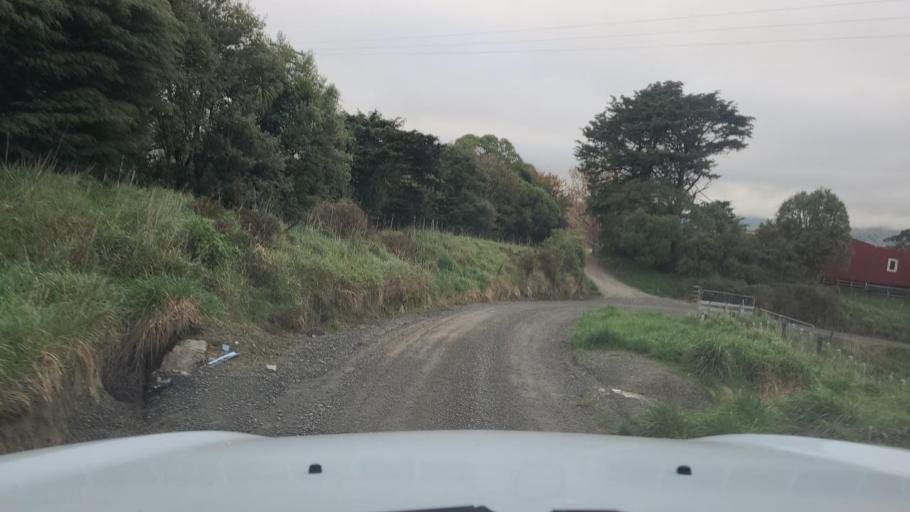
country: NZ
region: Wellington
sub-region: Masterton District
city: Masterton
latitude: -41.1610
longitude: 175.6839
